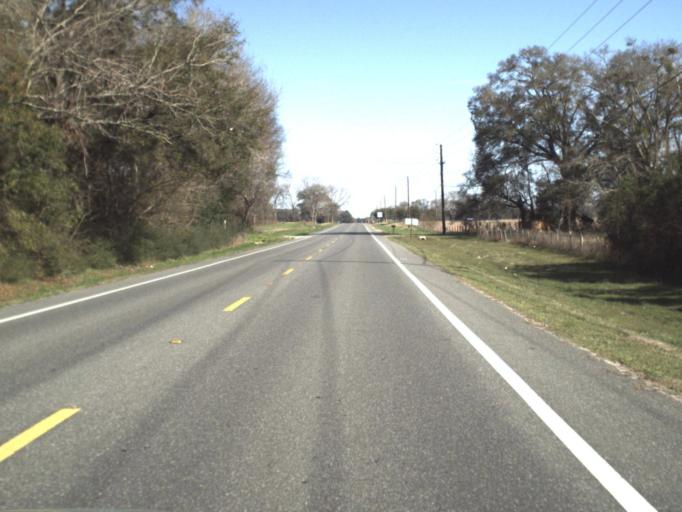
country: US
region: Florida
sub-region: Jackson County
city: Malone
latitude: 30.8979
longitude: -85.1611
